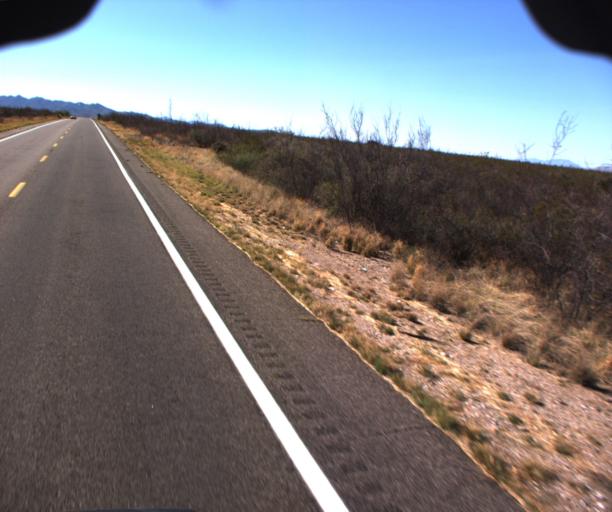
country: US
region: Arizona
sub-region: Cochise County
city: Tombstone
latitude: 31.6080
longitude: -110.0497
